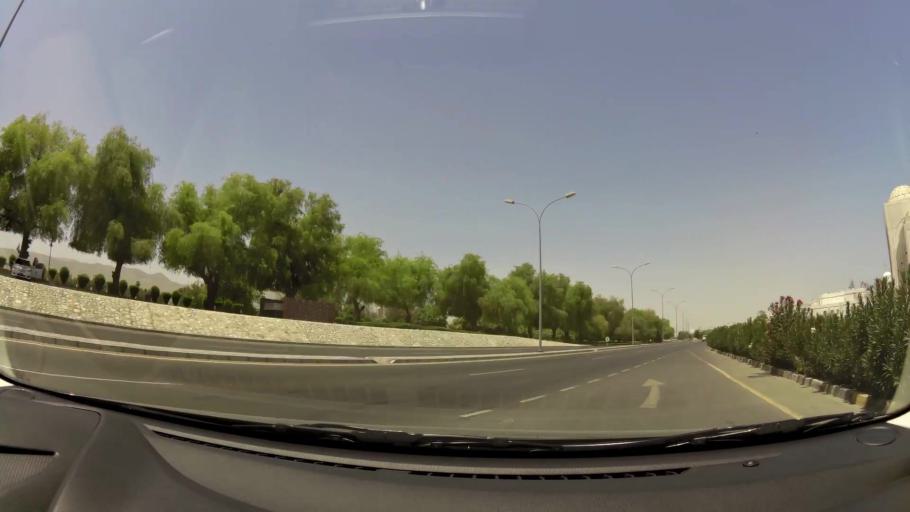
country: OM
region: Muhafazat Masqat
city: Bawshar
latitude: 23.6119
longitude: 58.4621
